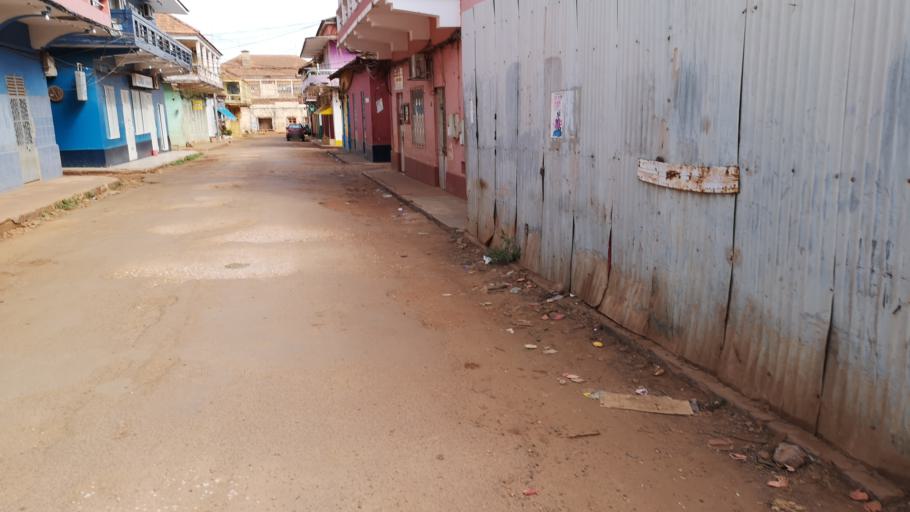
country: GW
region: Bissau
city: Bissau
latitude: 11.8595
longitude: -15.5797
